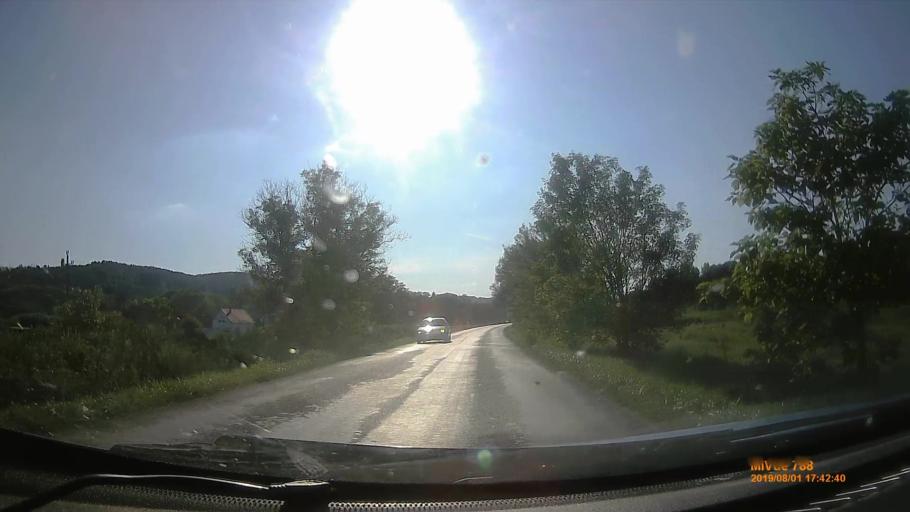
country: HU
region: Baranya
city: Sasd
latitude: 46.1907
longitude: 18.1583
